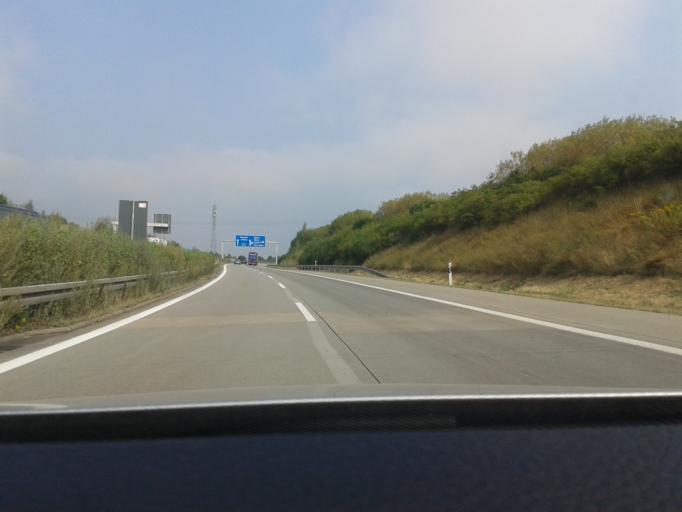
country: DE
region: Saxony
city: Freital
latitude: 51.0486
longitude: 13.6069
